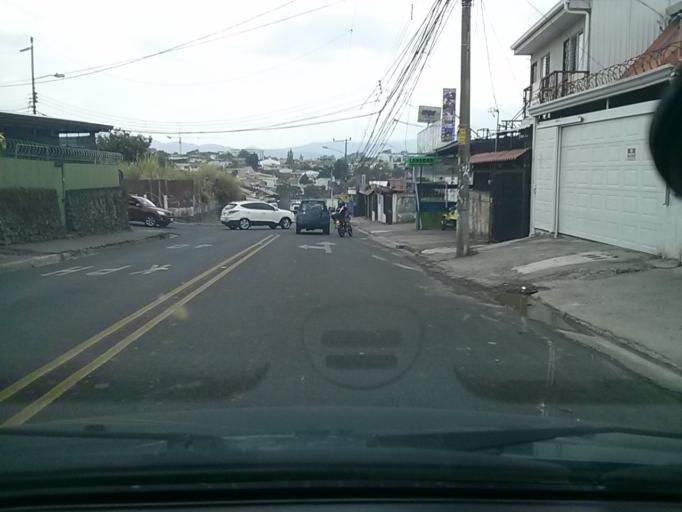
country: CR
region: San Jose
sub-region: Canton de Goicoechea
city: Guadalupe
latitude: 9.9452
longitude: -84.0518
